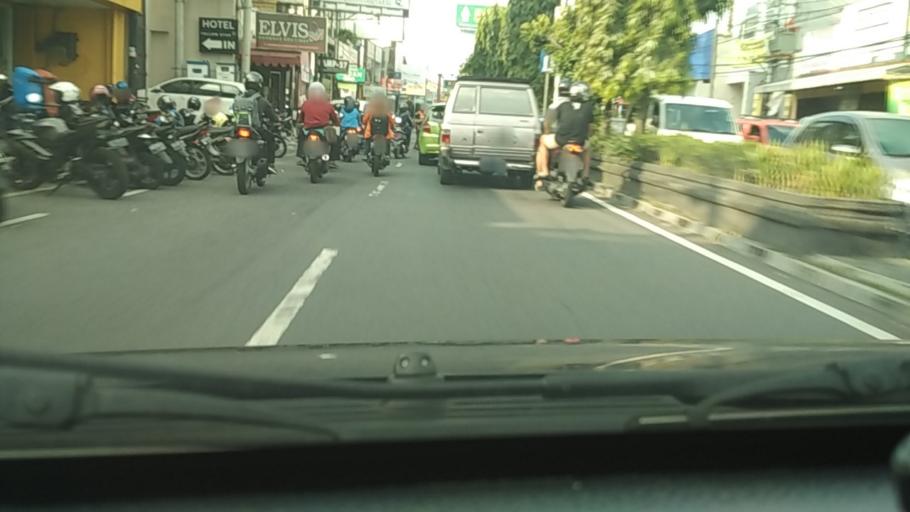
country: ID
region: Daerah Istimewa Yogyakarta
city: Yogyakarta
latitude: -7.7716
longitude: 110.3899
